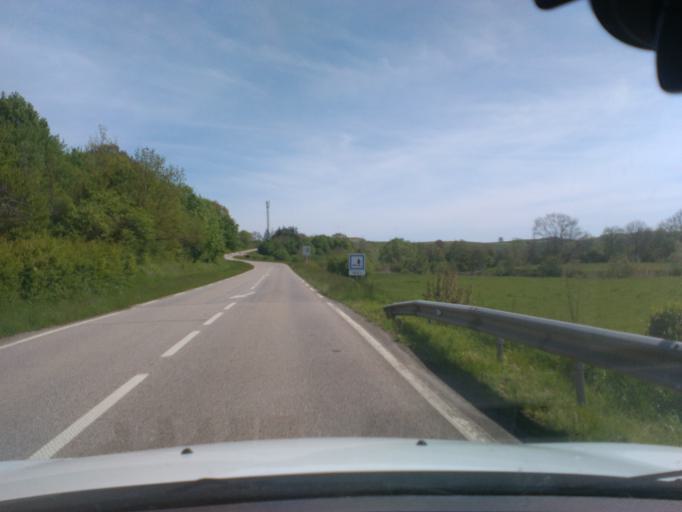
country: FR
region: Lorraine
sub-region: Departement des Vosges
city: Mirecourt
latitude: 48.3273
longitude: 6.1317
